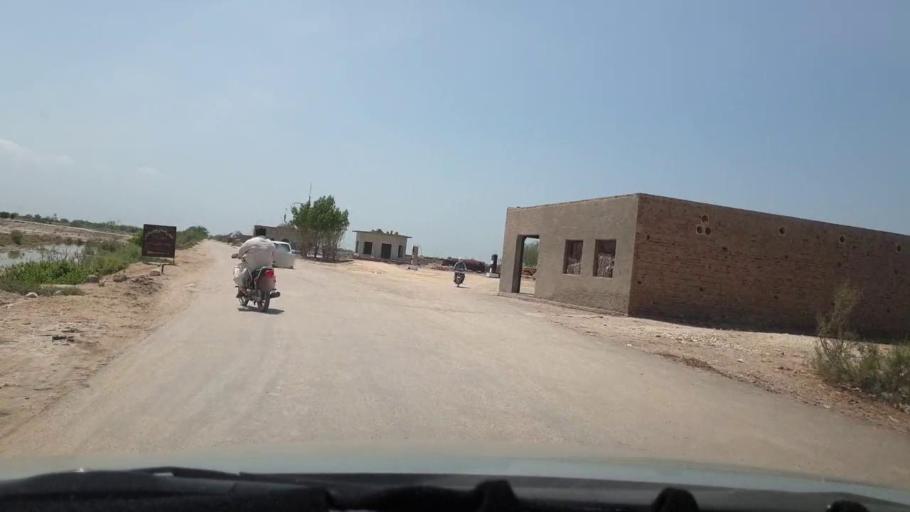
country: PK
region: Sindh
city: Pano Aqil
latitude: 27.6633
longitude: 69.1628
